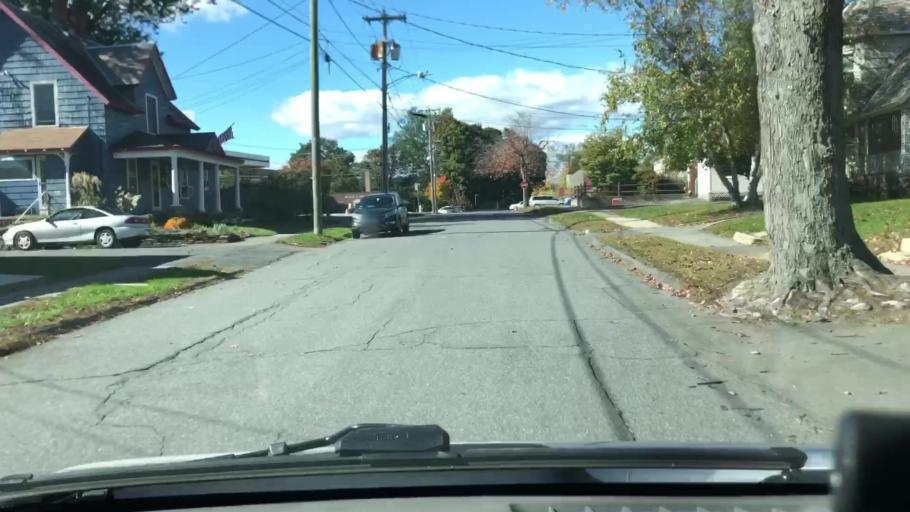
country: US
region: Massachusetts
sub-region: Franklin County
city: Greenfield
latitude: 42.5982
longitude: -72.5949
